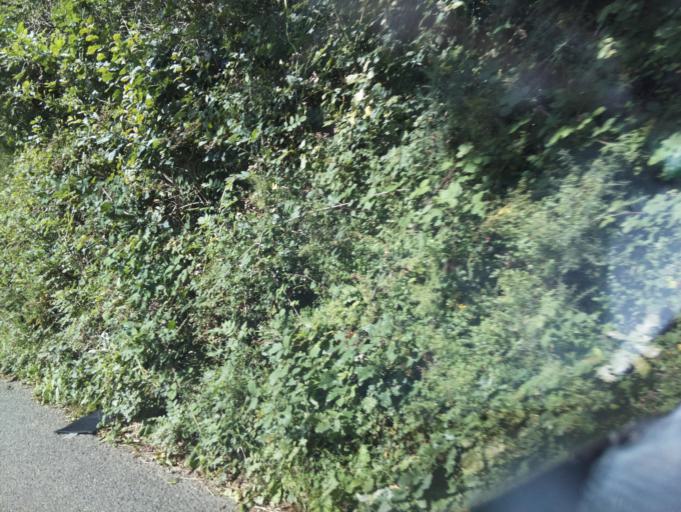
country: GB
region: England
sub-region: Devon
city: Ashburton
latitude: 50.5195
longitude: -3.7836
